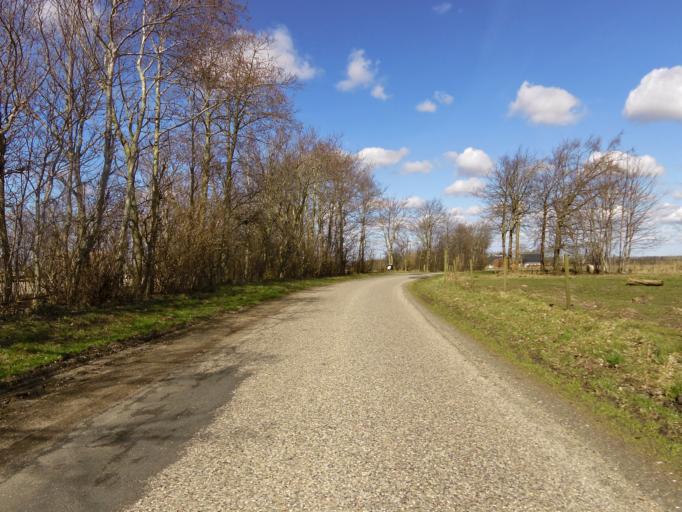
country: DK
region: South Denmark
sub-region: Tonder Kommune
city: Toftlund
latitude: 55.1857
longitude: 9.0943
